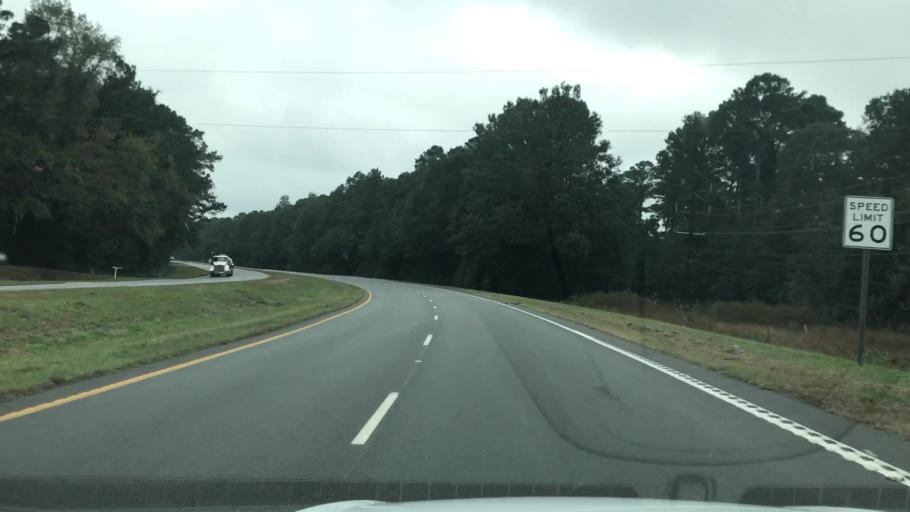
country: US
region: South Carolina
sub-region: Beaufort County
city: Laurel Bay
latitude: 32.5855
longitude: -80.7433
